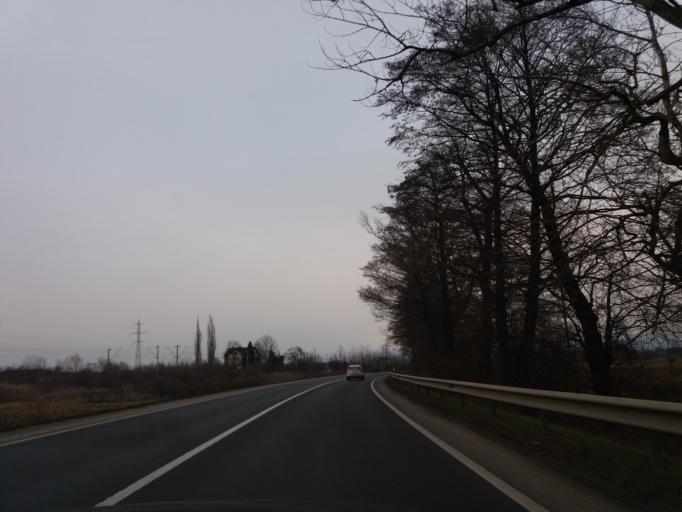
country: RO
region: Hunedoara
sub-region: Comuna Bacia
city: Bacia
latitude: 45.7900
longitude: 23.0013
